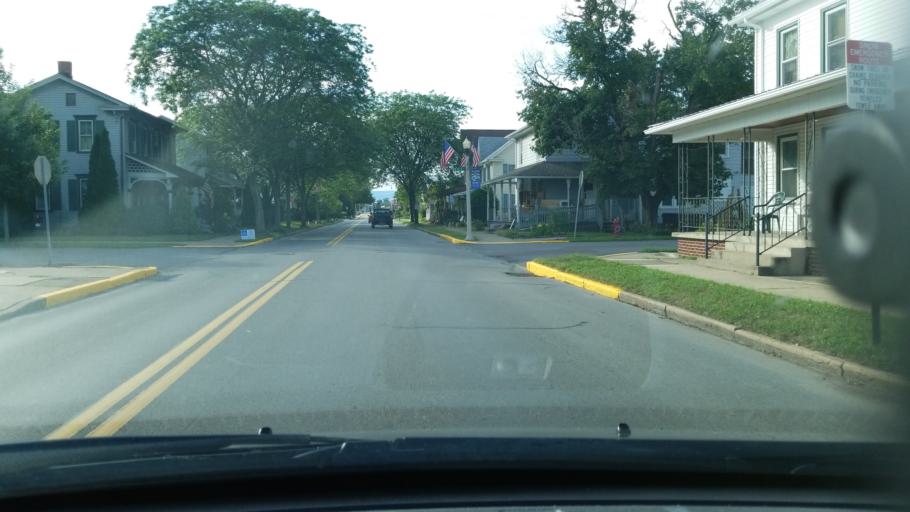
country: US
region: Pennsylvania
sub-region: Northumberland County
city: Watsontown
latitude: 41.0885
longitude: -76.8677
